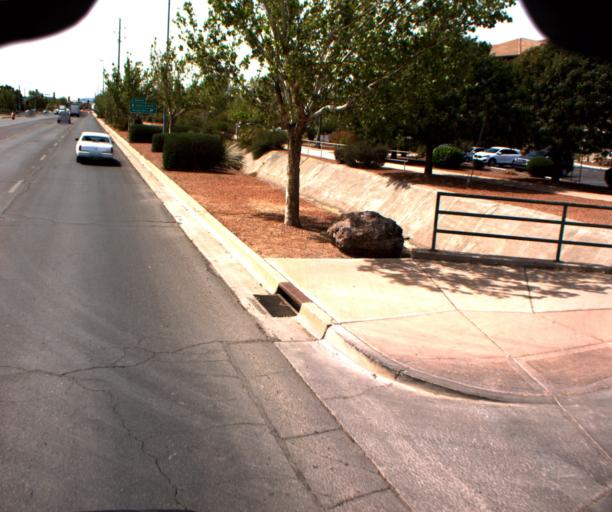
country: US
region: Arizona
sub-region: Cochise County
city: Douglas
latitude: 31.3413
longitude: -109.5583
